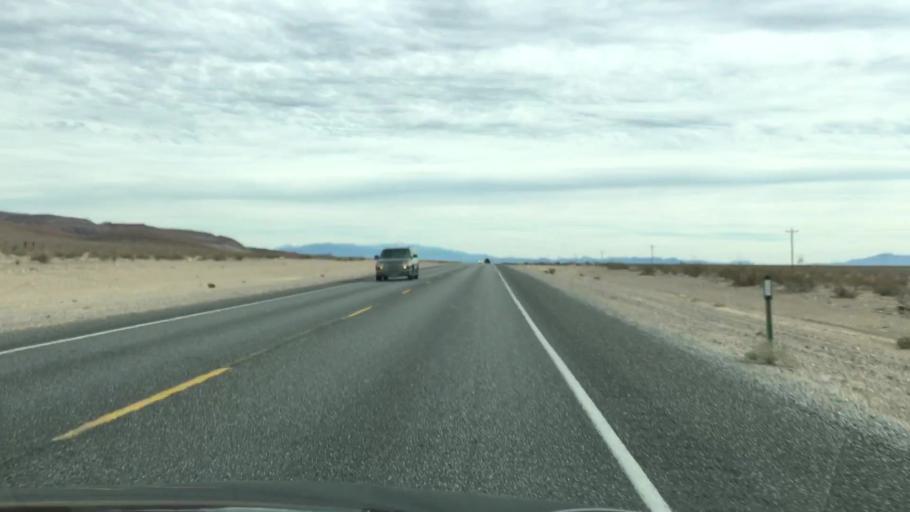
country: US
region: Nevada
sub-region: Nye County
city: Beatty
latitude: 36.7020
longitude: -116.5846
